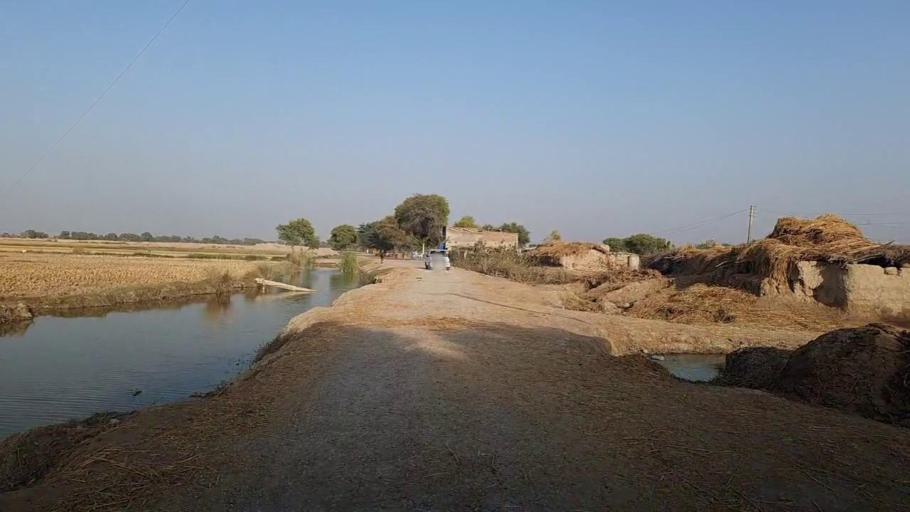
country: PK
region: Sindh
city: Kashmor
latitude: 28.4256
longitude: 69.4314
